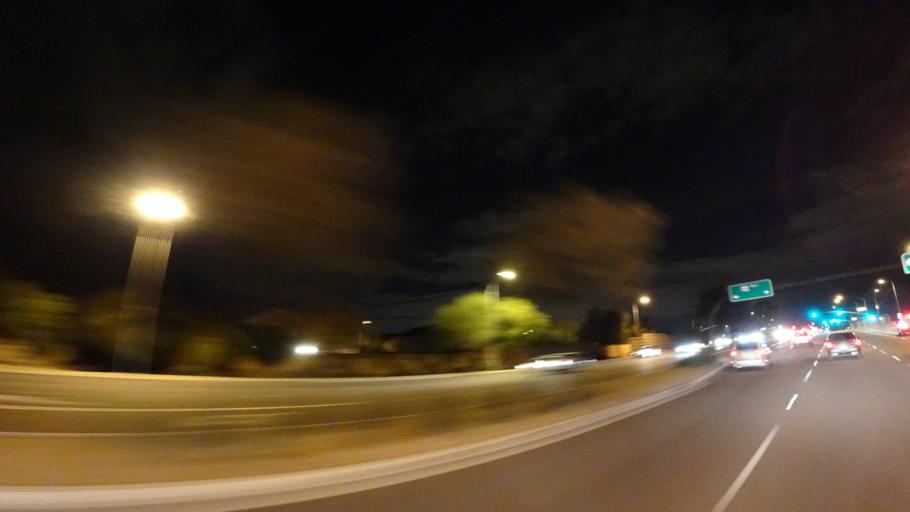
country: US
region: Arizona
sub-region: Maricopa County
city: Chandler
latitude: 33.2854
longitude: -111.8589
